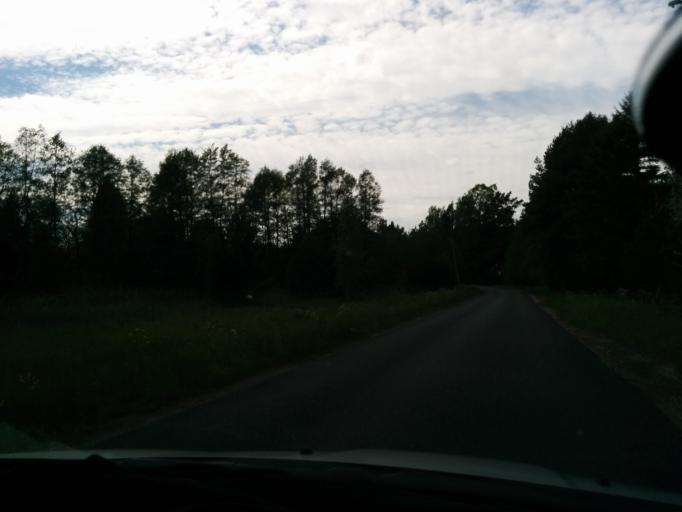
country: EE
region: Harju
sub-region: Loksa linn
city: Loksa
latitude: 59.5631
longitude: 25.6856
